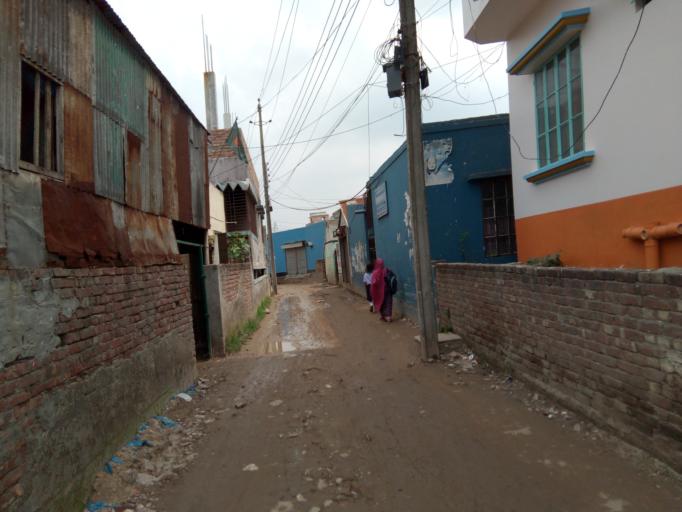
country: BD
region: Dhaka
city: Paltan
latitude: 23.7517
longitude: 90.4496
